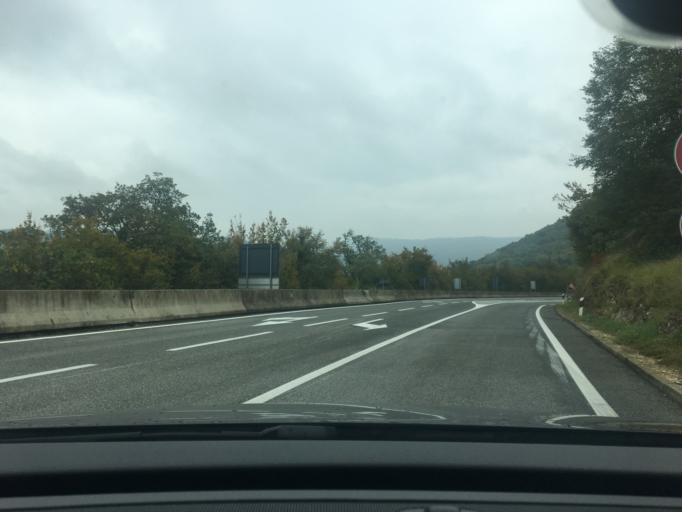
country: HR
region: Istarska
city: Buje
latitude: 45.4540
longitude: 13.6447
